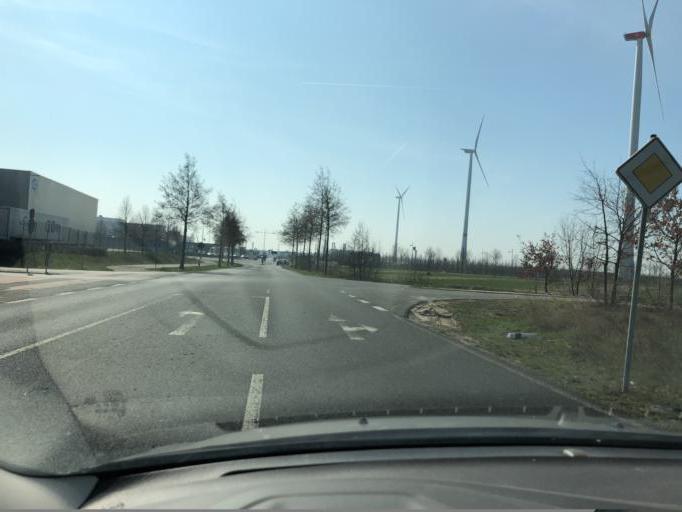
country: DE
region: Saxony
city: Krostitz
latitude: 51.4137
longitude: 12.4372
